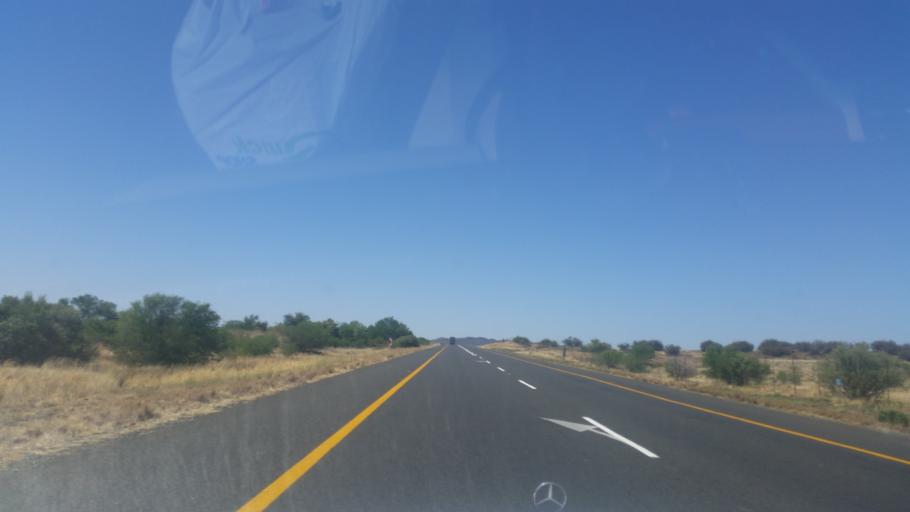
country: ZA
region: Northern Cape
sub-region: Pixley ka Seme District Municipality
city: Colesberg
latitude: -30.5735
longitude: 25.4480
